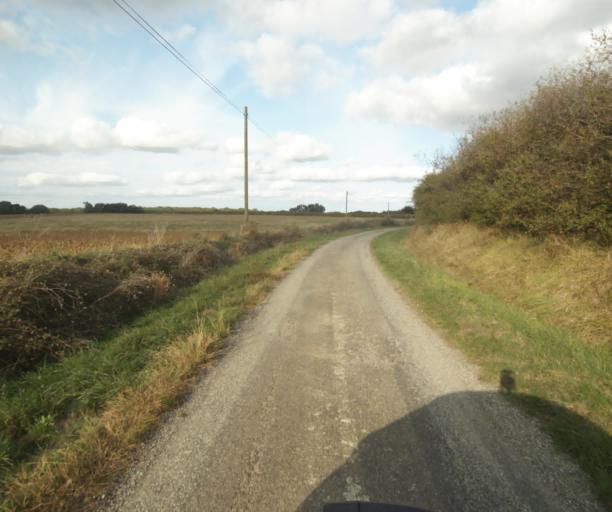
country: FR
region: Midi-Pyrenees
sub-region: Departement de la Haute-Garonne
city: Launac
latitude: 43.8261
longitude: 1.1080
